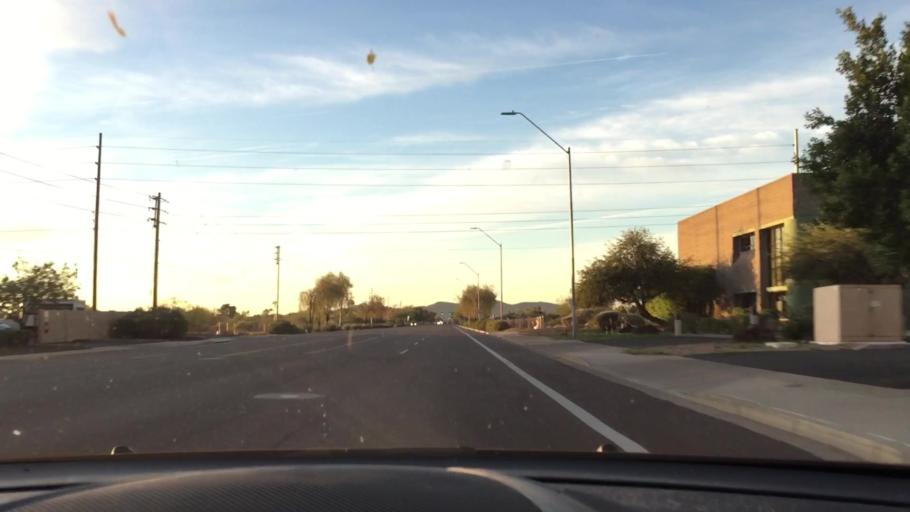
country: US
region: Arizona
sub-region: Maricopa County
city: Glendale
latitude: 33.6808
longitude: -112.0830
